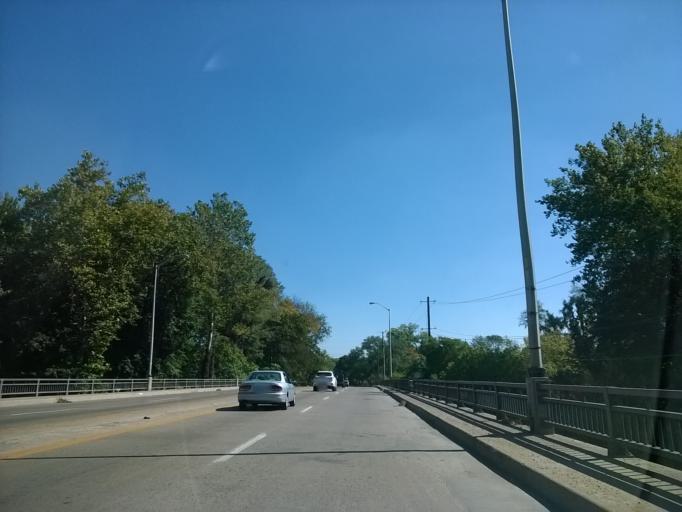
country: US
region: Indiana
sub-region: Marion County
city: Broad Ripple
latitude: 39.8621
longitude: -86.1621
